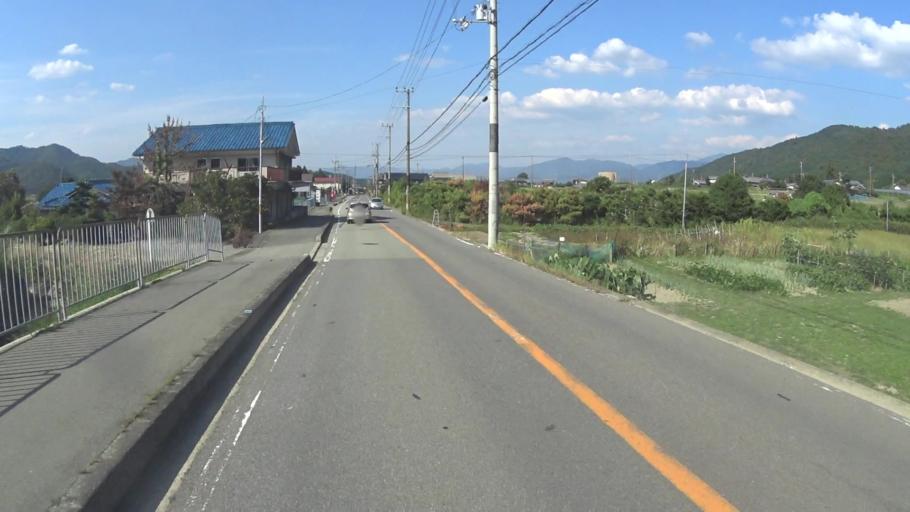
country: JP
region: Kyoto
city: Kameoka
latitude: 34.9849
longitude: 135.5467
